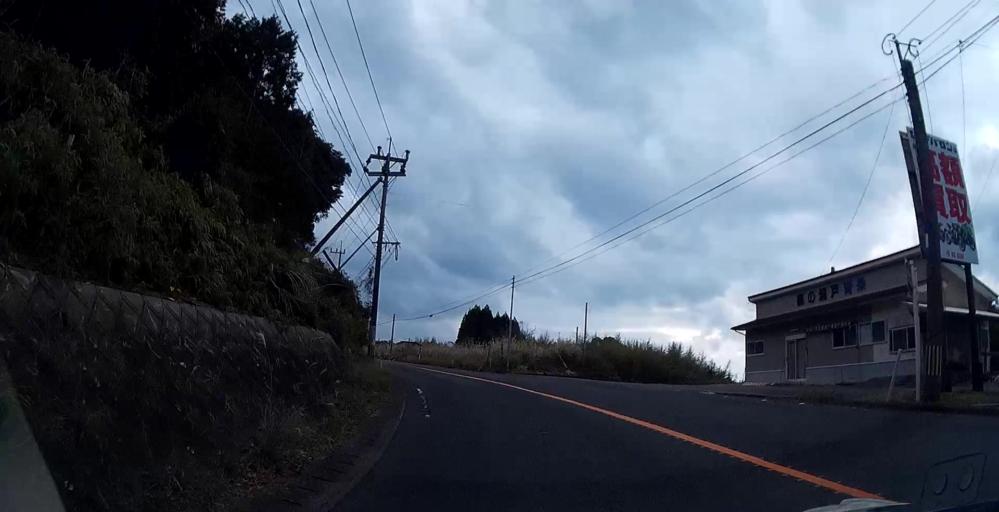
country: JP
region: Kagoshima
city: Akune
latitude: 32.0997
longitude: 130.1763
